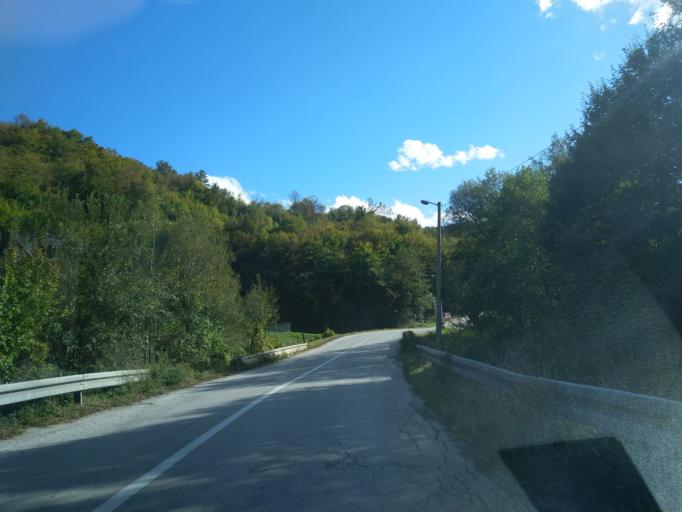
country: RS
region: Central Serbia
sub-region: Zlatiborski Okrug
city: Uzice
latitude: 43.8863
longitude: 19.7782
